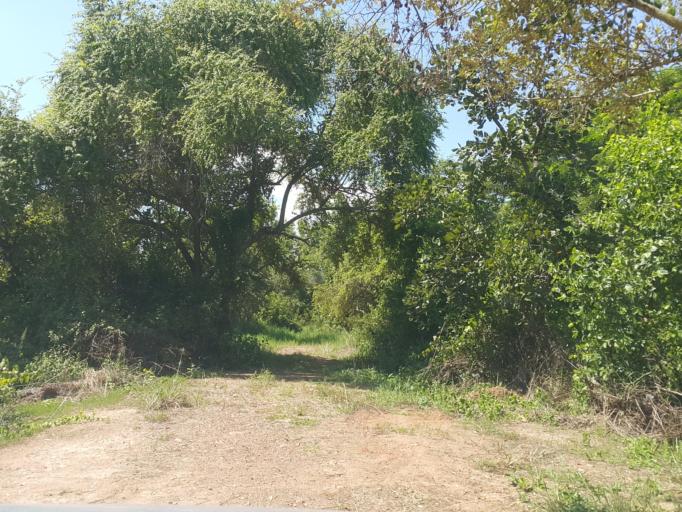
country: TH
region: Chiang Mai
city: Saraphi
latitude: 18.7646
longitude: 99.0596
